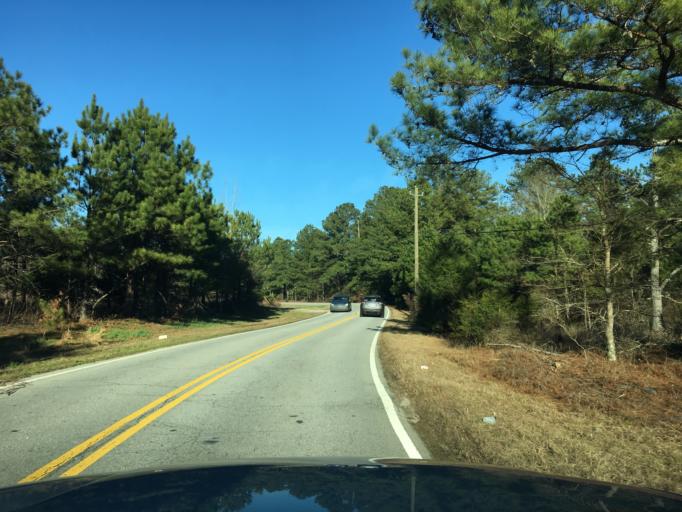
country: US
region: Georgia
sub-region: Rockdale County
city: Lakeview Estates
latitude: 33.6977
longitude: -84.0403
